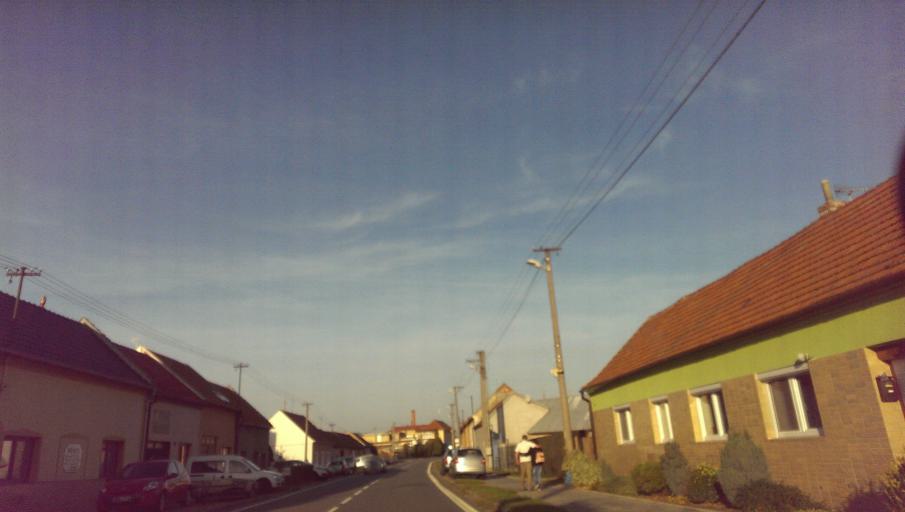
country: CZ
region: Zlin
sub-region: Okres Zlin
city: Ostrozska Nova Ves
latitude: 48.9982
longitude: 17.4300
